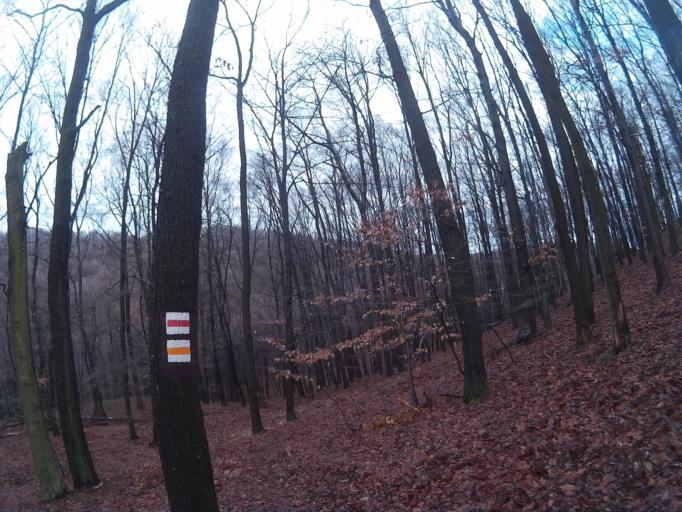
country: HU
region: Nograd
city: Somoskoujfalu
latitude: 48.1531
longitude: 19.7933
